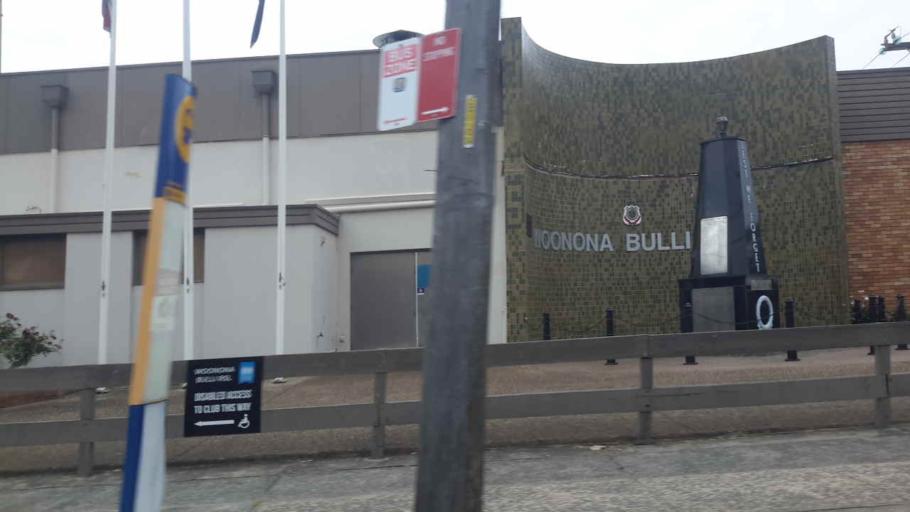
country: AU
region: New South Wales
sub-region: Wollongong
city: Bulli
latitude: -34.3439
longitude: 150.9044
